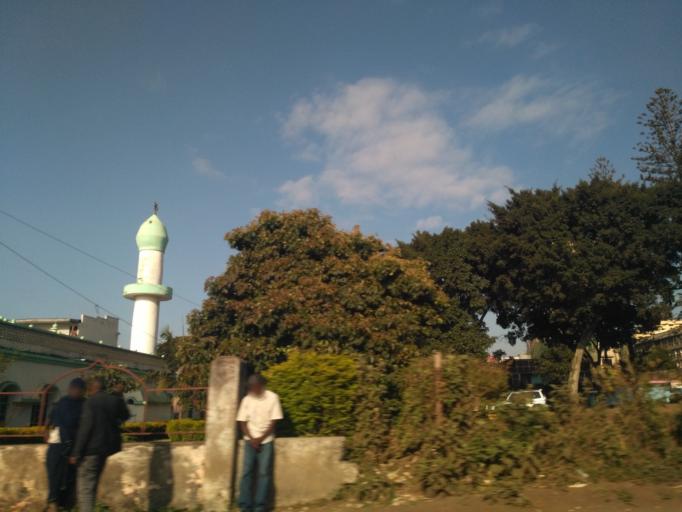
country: TZ
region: Arusha
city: Arusha
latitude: -3.3707
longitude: 36.6882
